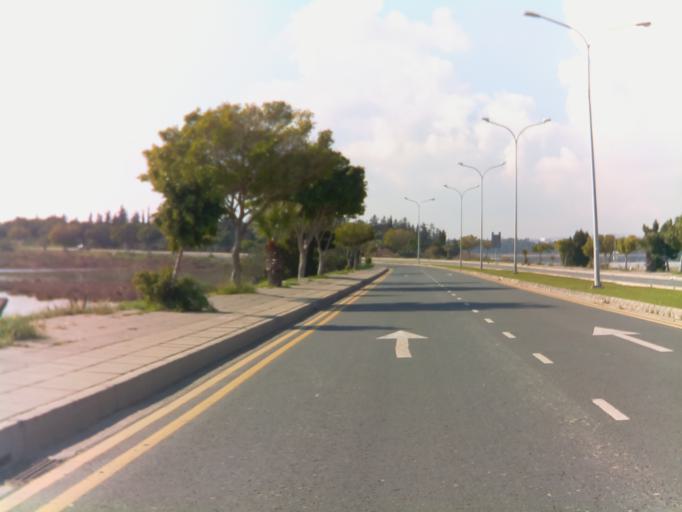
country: CY
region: Larnaka
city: Larnaca
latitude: 34.8867
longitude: 33.6250
